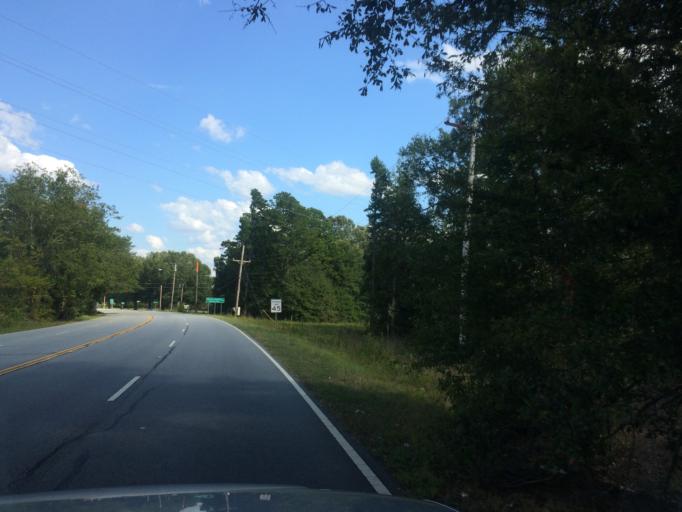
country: US
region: South Carolina
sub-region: Anderson County
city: Honea Path
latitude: 34.4459
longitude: -82.3761
